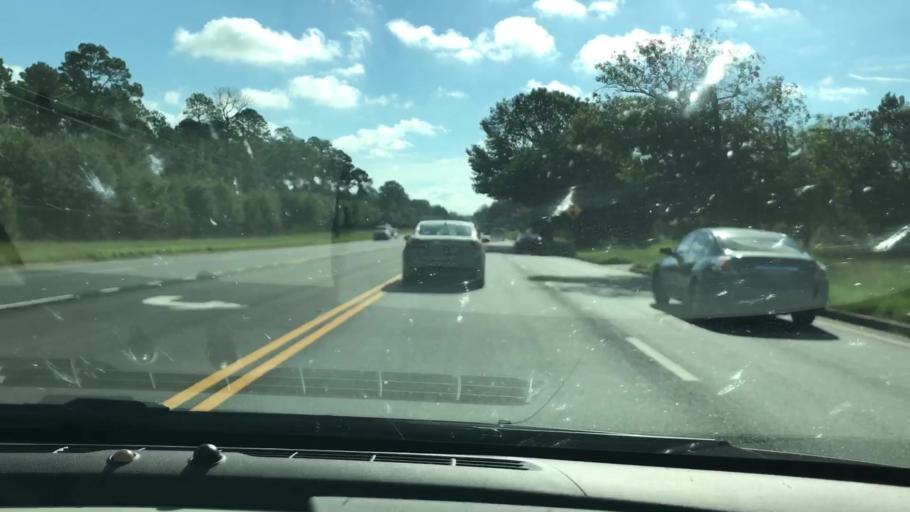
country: US
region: Georgia
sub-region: Dougherty County
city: Albany
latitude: 31.5799
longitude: -84.0975
